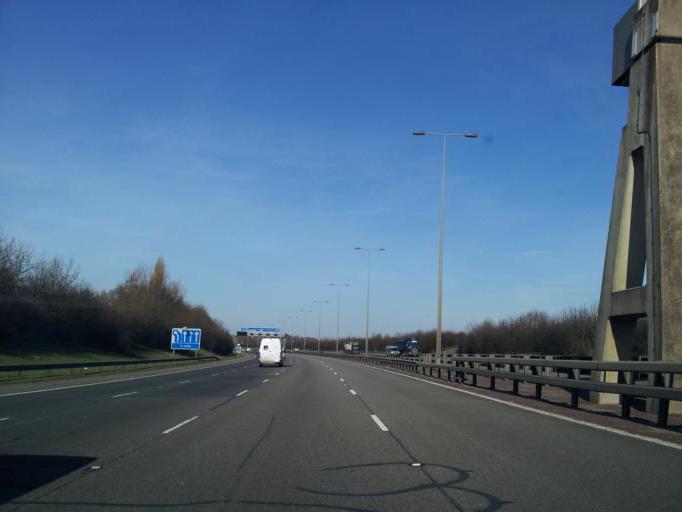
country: GB
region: England
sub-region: Cambridgeshire
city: Stilton
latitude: 52.4873
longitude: -0.2850
